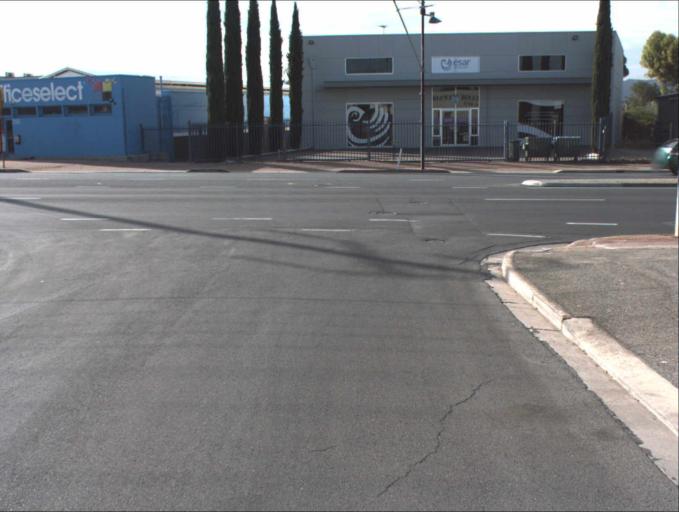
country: AU
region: South Australia
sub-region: Port Adelaide Enfield
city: Klemzig
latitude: -34.8727
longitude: 138.6347
